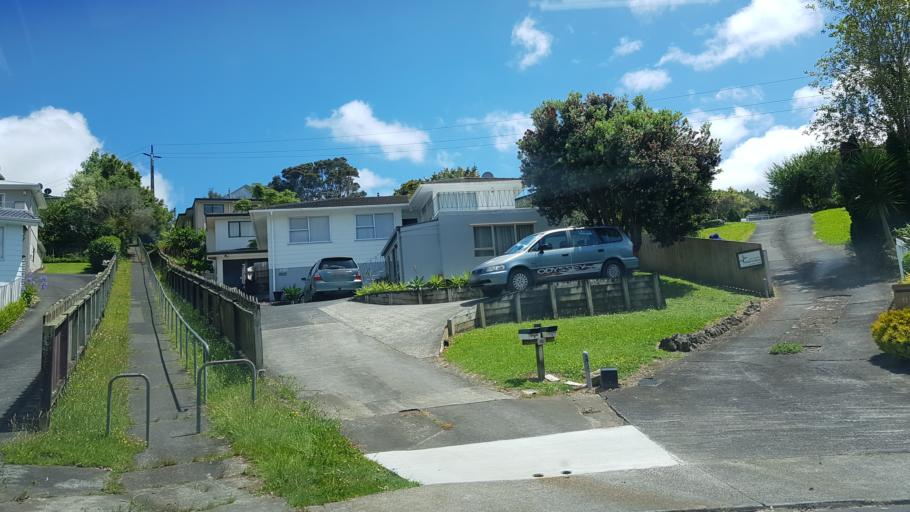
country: NZ
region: Auckland
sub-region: Auckland
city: North Shore
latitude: -36.7787
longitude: 174.7139
